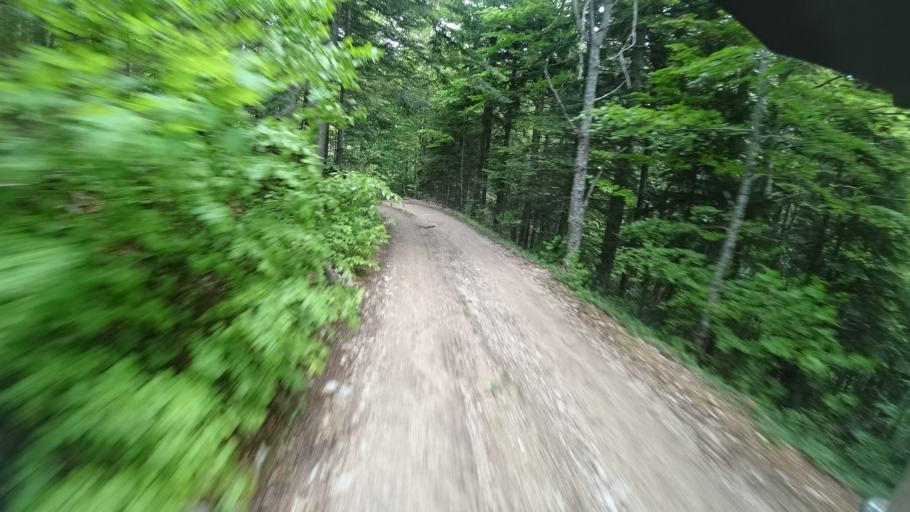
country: BA
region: Federation of Bosnia and Herzegovina
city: Bihac
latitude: 44.6798
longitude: 15.8466
